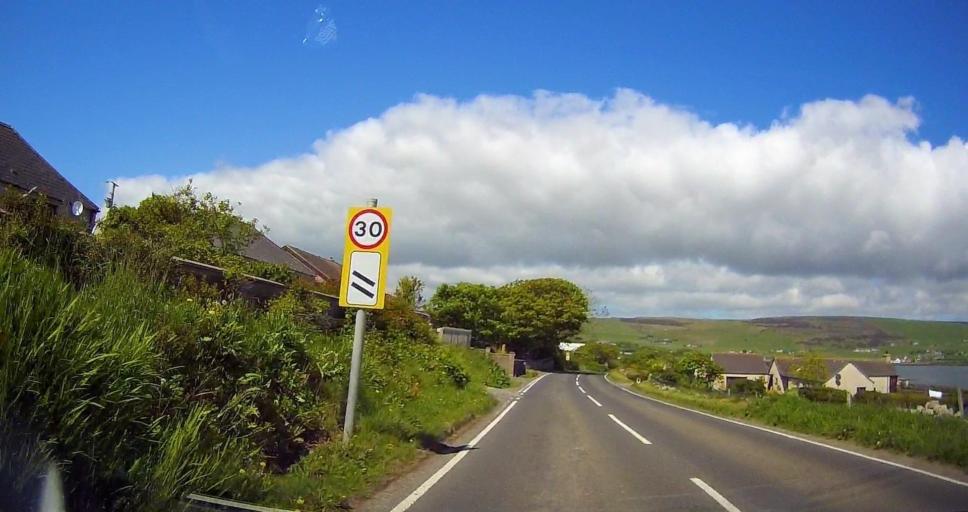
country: GB
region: Scotland
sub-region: Orkney Islands
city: Orkney
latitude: 59.0002
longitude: -3.1029
